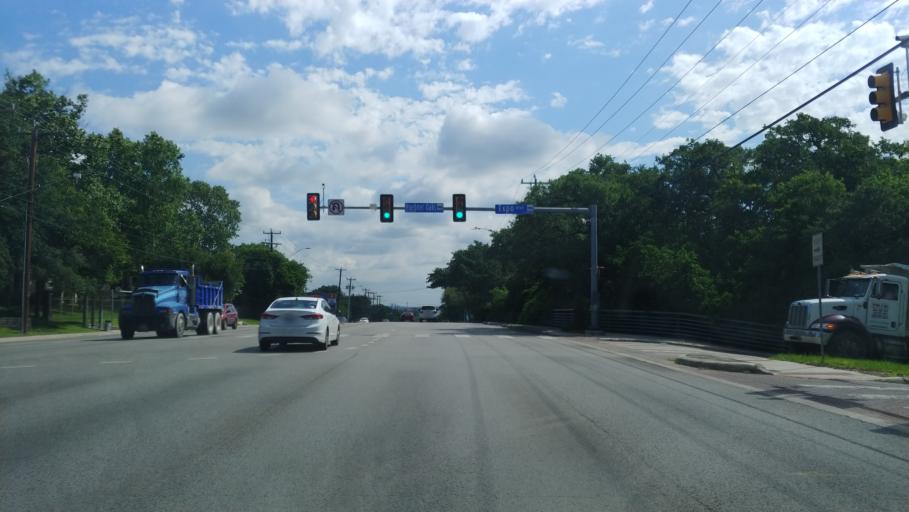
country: US
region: Texas
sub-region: Bexar County
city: Shavano Park
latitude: 29.5469
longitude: -98.5764
